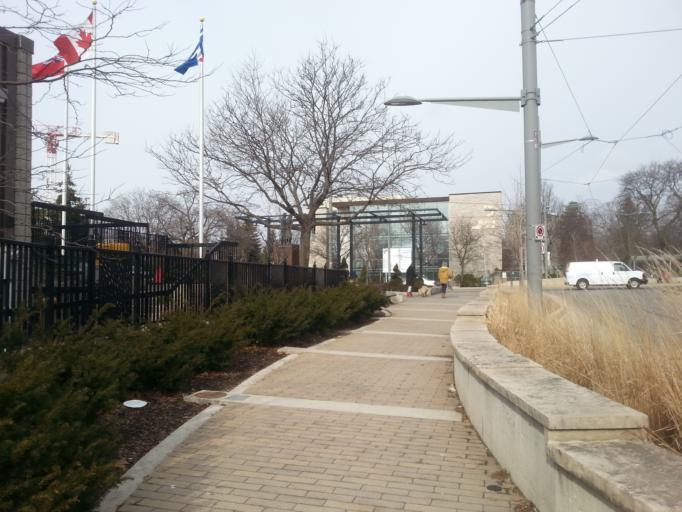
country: CA
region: Ontario
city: Toronto
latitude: 43.6757
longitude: -79.4510
